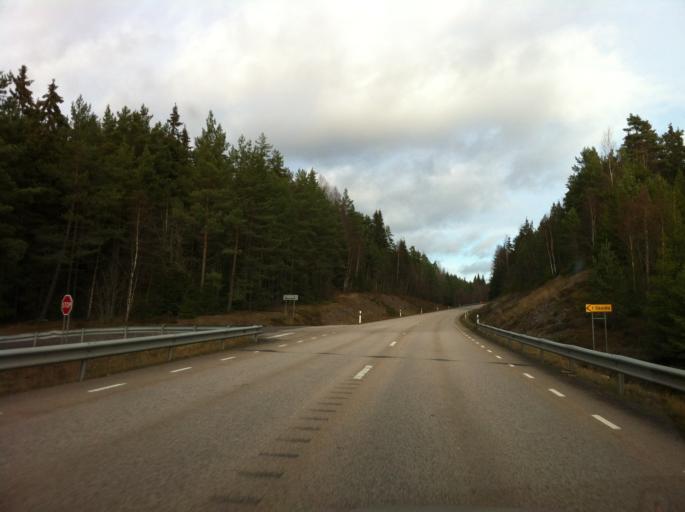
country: SE
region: Kronoberg
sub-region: Uppvidinge Kommun
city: Lenhovda
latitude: 57.0920
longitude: 15.1933
